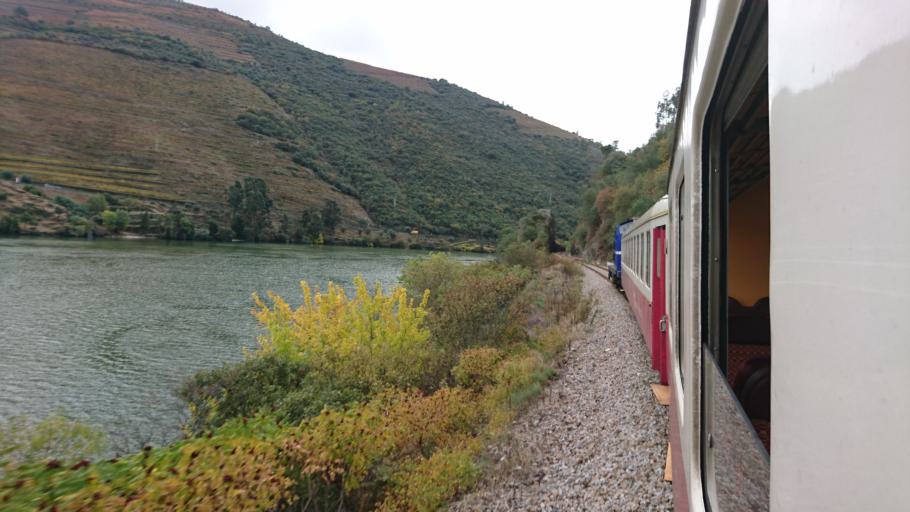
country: PT
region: Viseu
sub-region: Tabuaco
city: Tabuaco
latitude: 41.1641
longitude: -7.5749
